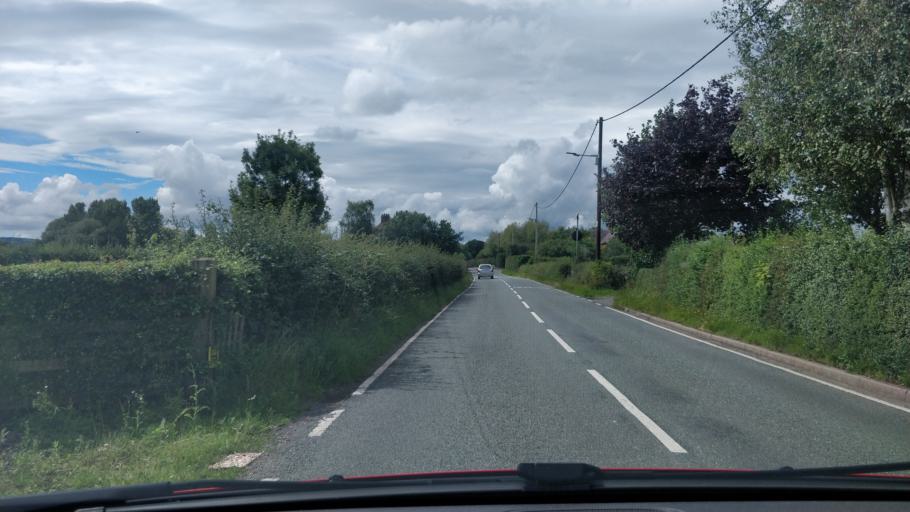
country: GB
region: Wales
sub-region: County of Flintshire
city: Hawarden
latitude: 53.1523
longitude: -2.9821
